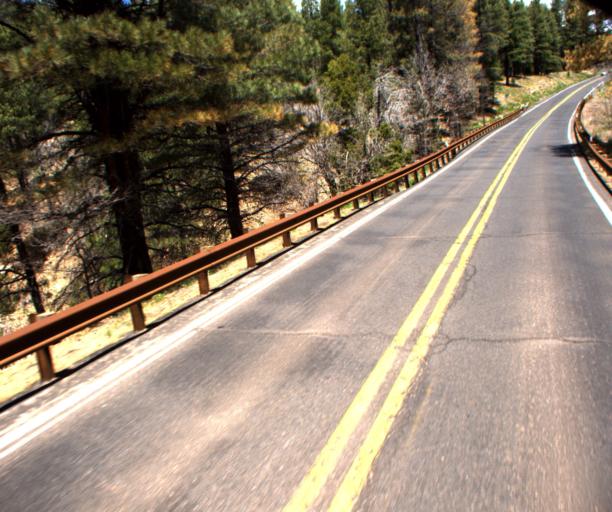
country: US
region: Arizona
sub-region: Coconino County
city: Kachina Village
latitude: 35.0643
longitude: -111.7330
